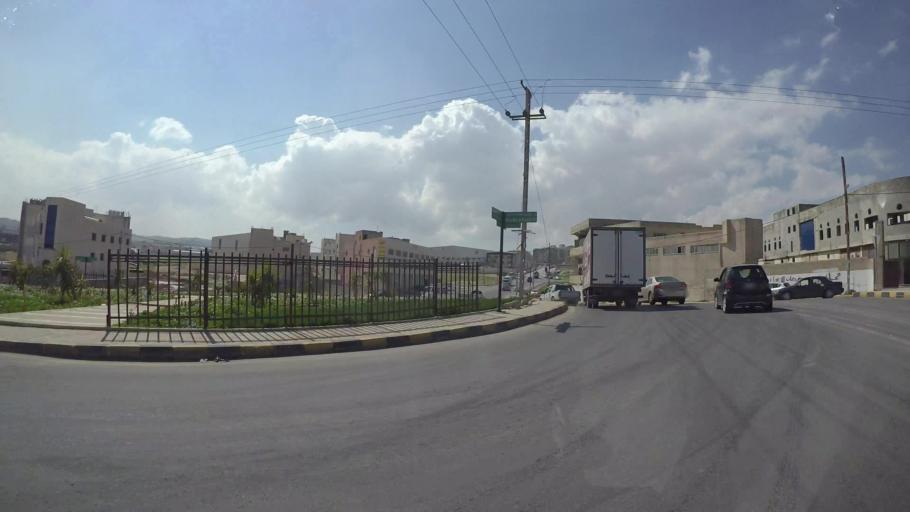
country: JO
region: Zarqa
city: Russeifa
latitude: 31.9926
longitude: 36.0126
